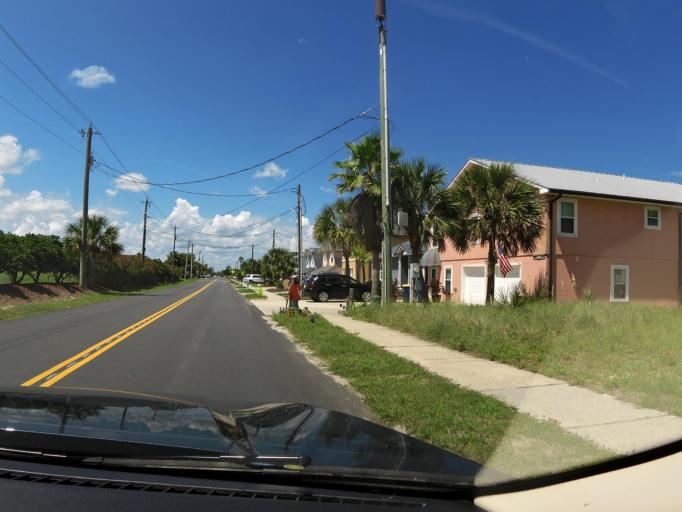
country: US
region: Florida
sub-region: Nassau County
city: Fernandina Beach
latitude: 30.6718
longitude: -81.4318
